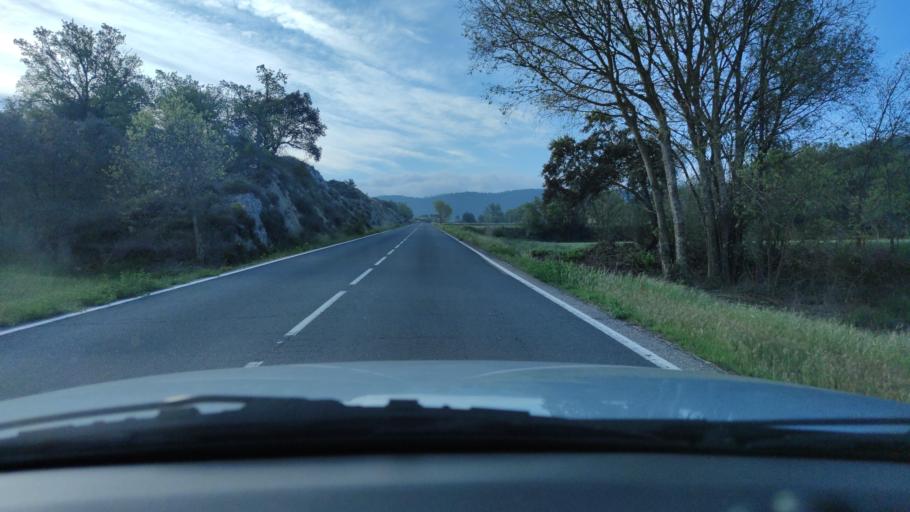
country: ES
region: Catalonia
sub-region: Provincia de Lleida
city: Ponts
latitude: 41.8938
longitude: 1.1758
